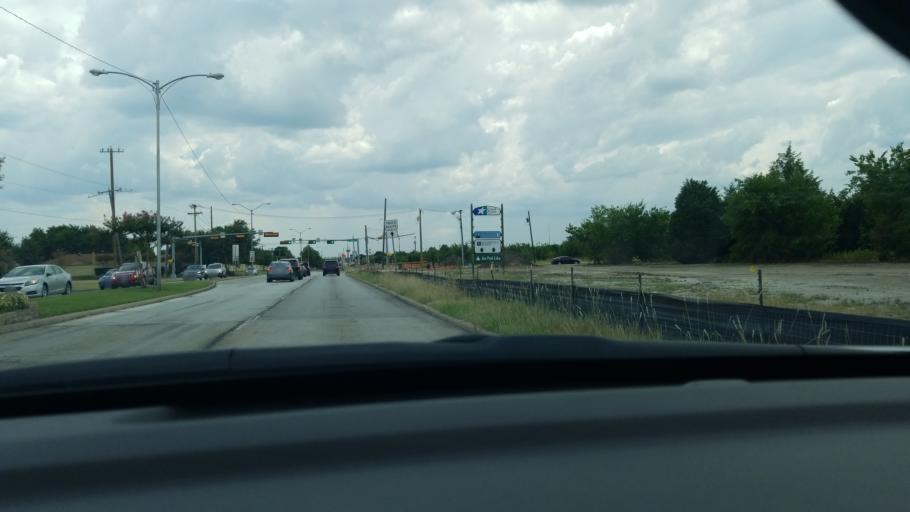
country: US
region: Texas
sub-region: Dallas County
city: Grand Prairie
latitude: 32.6851
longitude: -97.0443
